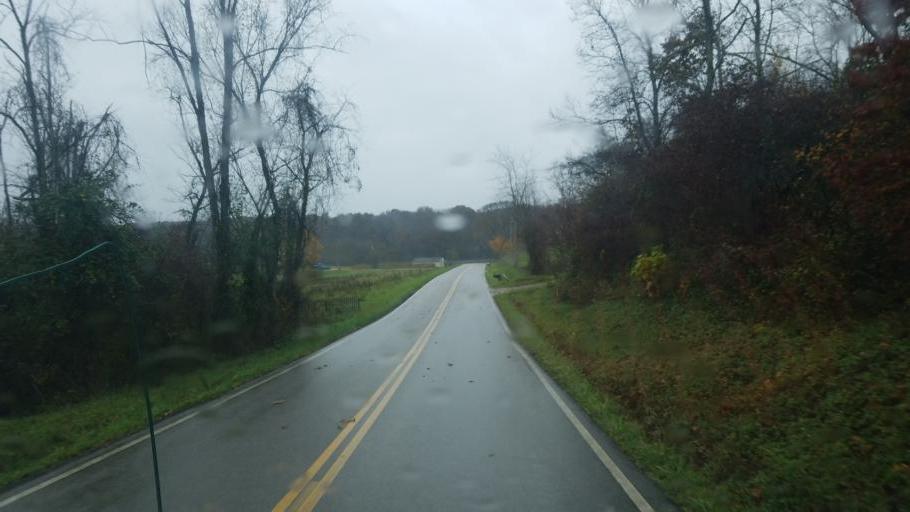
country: US
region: West Virginia
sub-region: Wood County
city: Blennerhassett
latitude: 39.3309
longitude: -81.6213
